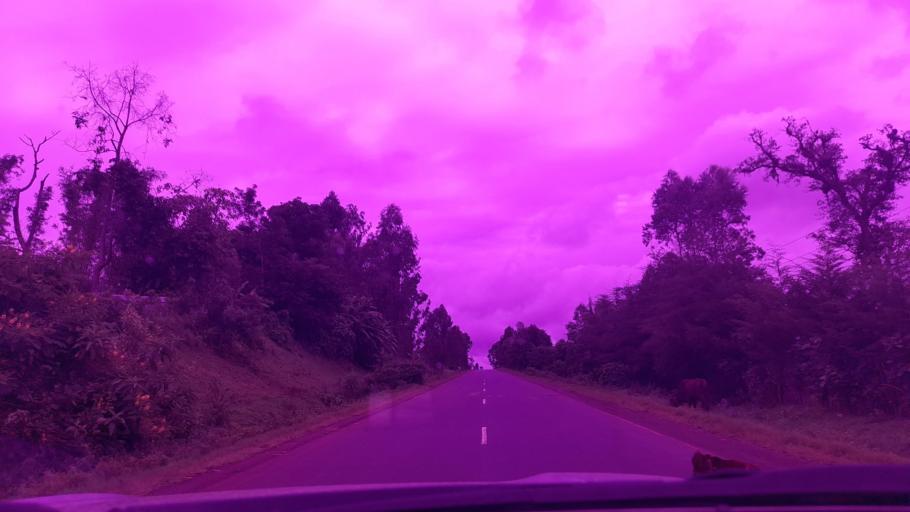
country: ET
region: Southern Nations, Nationalities, and People's Region
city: Bonga
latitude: 7.3034
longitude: 35.9943
